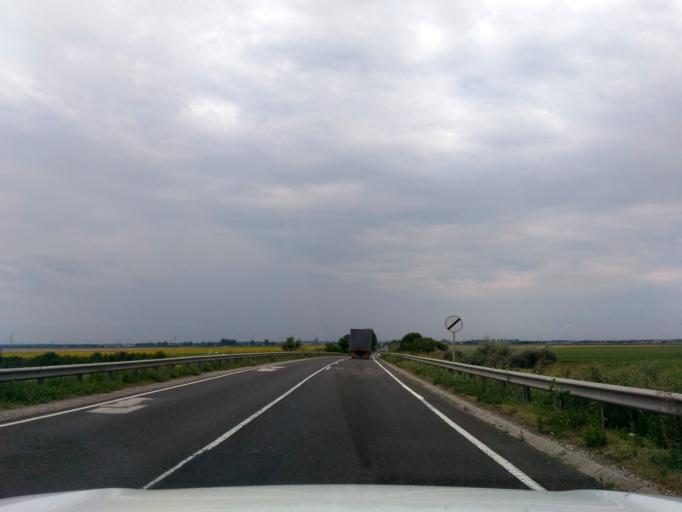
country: HU
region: Jasz-Nagykun-Szolnok
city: Toszeg
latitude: 47.1749
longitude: 20.1023
